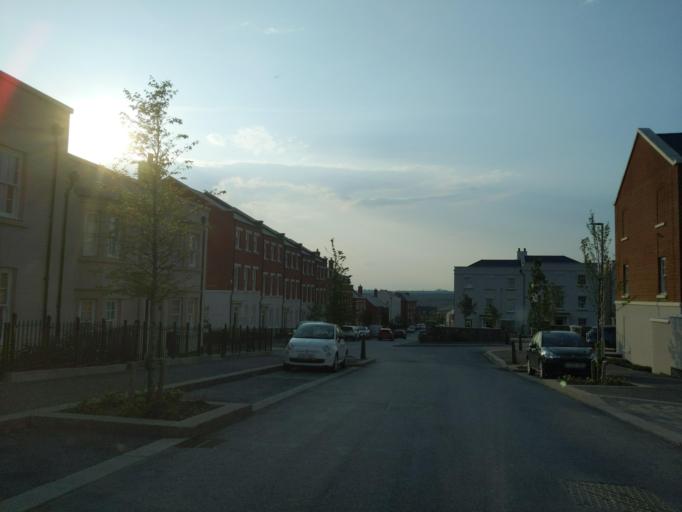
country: GB
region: England
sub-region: Devon
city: Plympton
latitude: 50.3633
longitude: -4.0497
